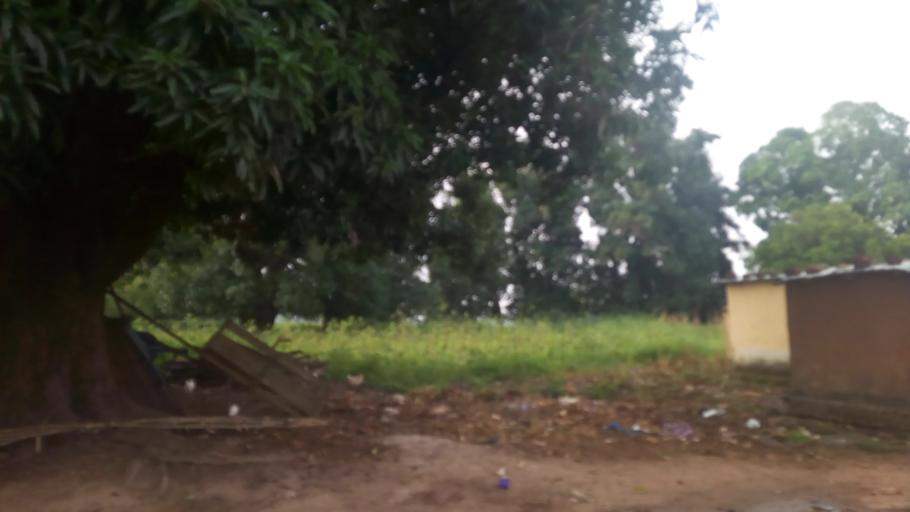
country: ML
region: Koulikoro
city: Kangaba
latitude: 11.6594
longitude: -8.7291
